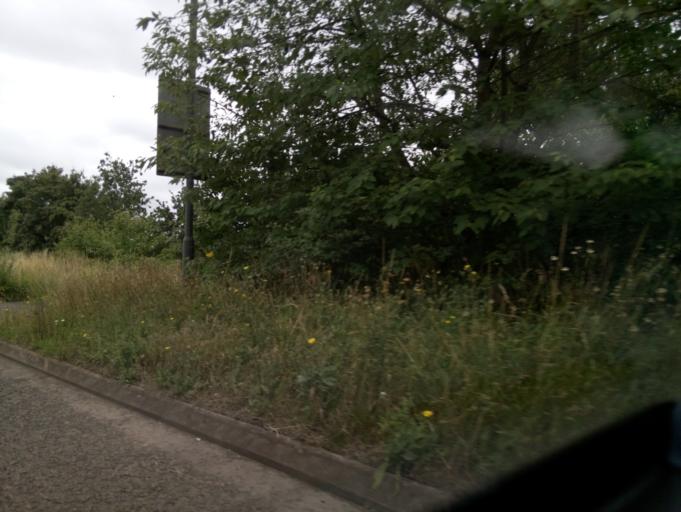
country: GB
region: England
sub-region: Gloucestershire
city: Tewkesbury
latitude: 51.9897
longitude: -2.1465
